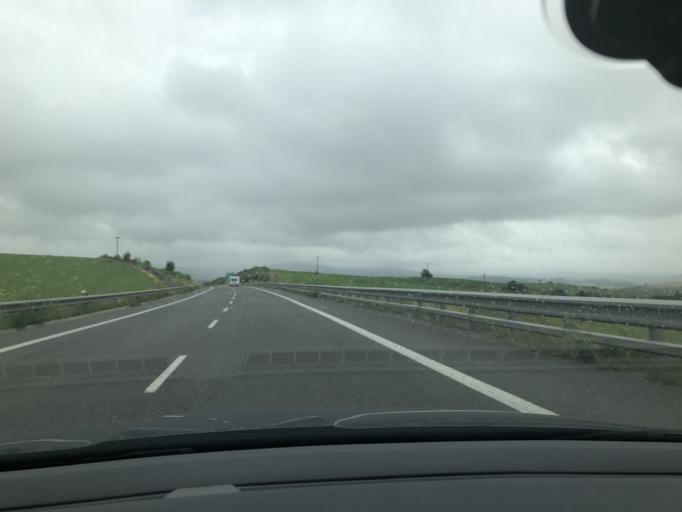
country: SK
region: Zilinsky
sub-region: Okres Zilina
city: Trstena
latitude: 49.3703
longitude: 19.6305
